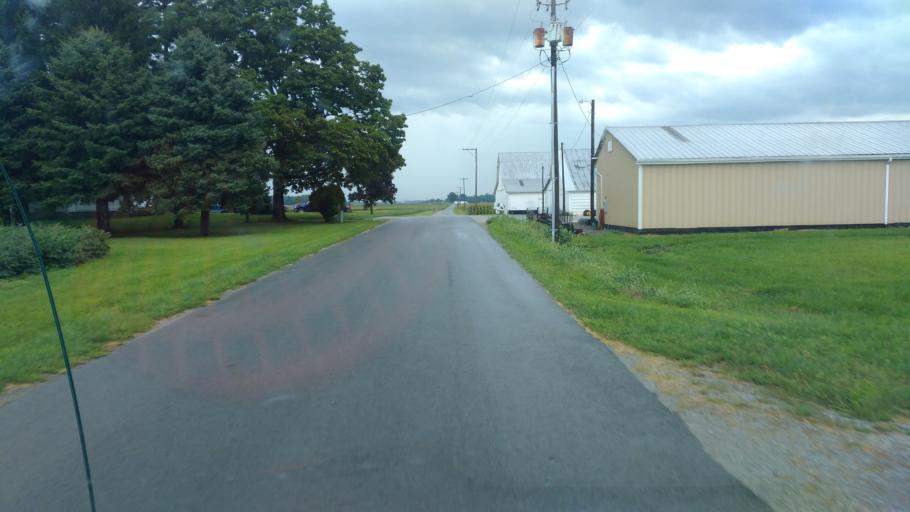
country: US
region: Ohio
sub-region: Hardin County
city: Kenton
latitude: 40.6893
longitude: -83.6286
